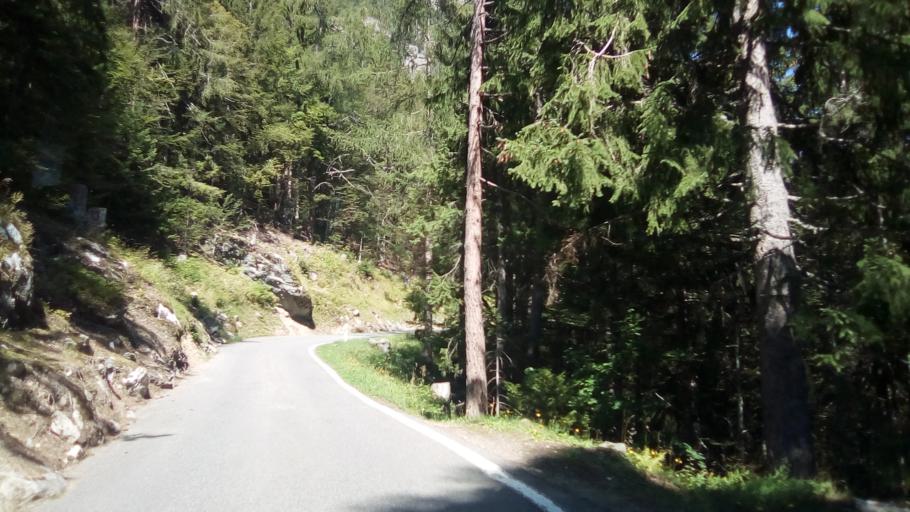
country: CH
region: Valais
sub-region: Saint-Maurice District
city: Salvan
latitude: 46.1321
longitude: 7.0192
